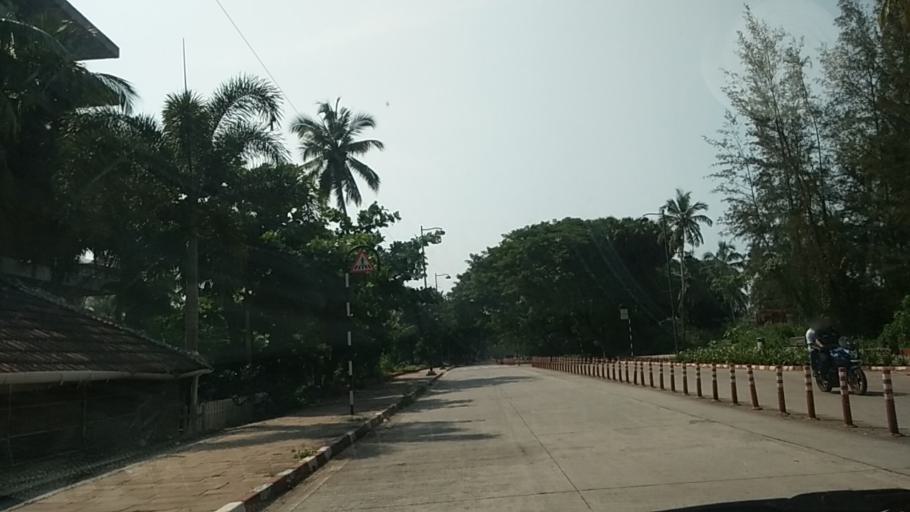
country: IN
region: Goa
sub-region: North Goa
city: Taleigao
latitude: 15.4710
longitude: 73.8079
